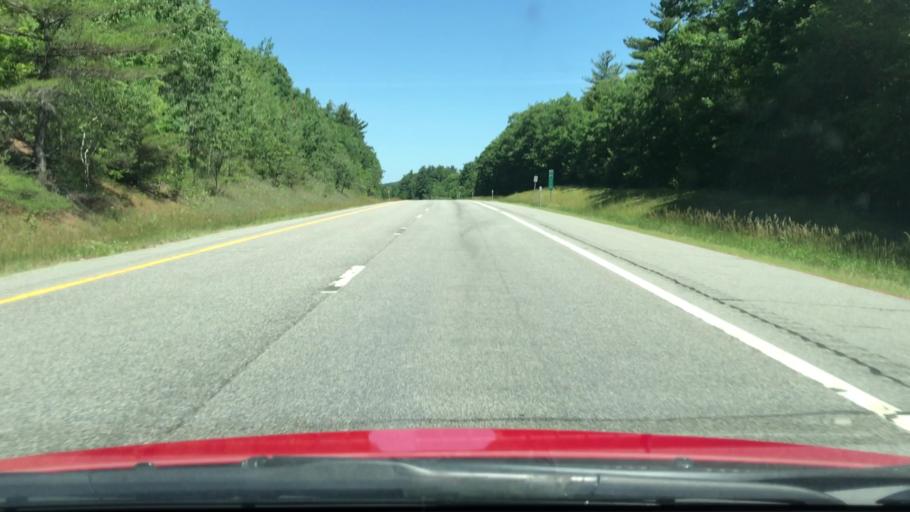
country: US
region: New York
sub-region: Essex County
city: Mineville
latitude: 44.1353
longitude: -73.5862
